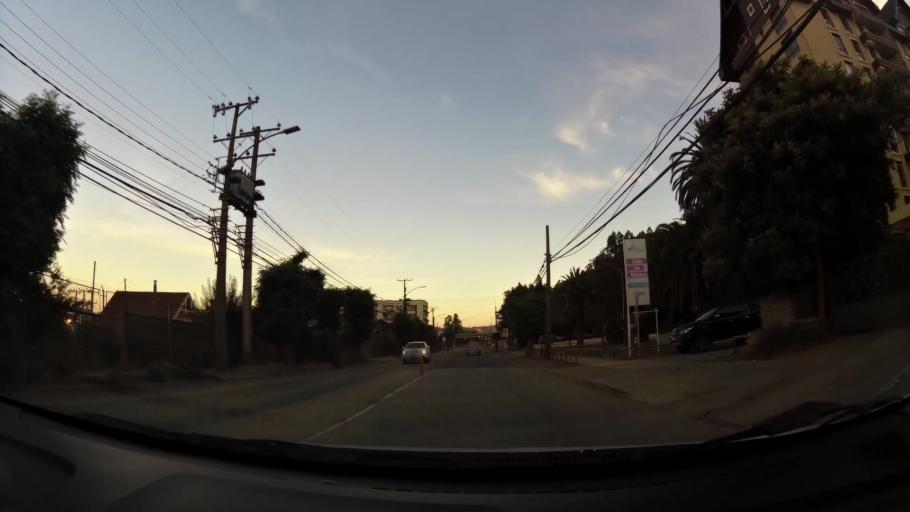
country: CL
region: Biobio
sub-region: Provincia de Concepcion
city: Concepcion
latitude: -36.8421
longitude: -73.0793
